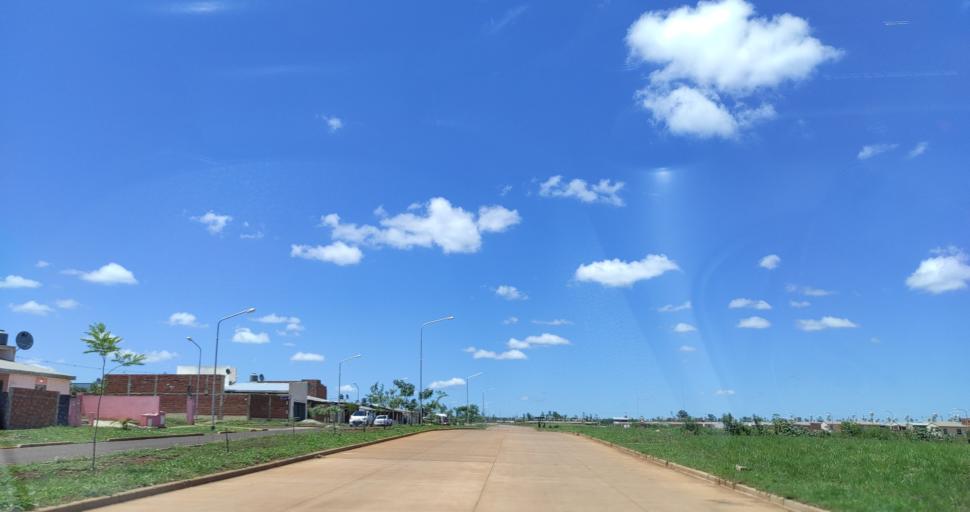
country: AR
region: Misiones
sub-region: Departamento de Capital
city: Posadas
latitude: -27.4088
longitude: -55.9880
